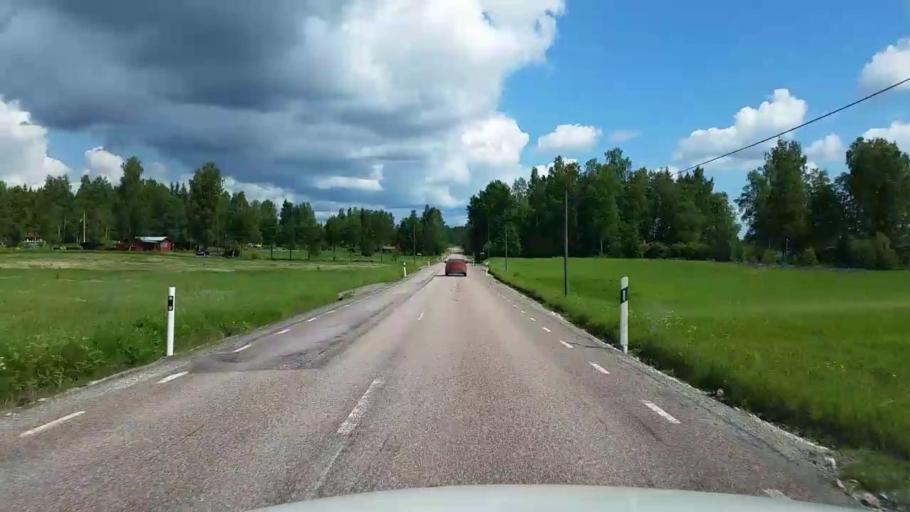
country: SE
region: Vaestmanland
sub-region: Skinnskattebergs Kommun
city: Skinnskatteberg
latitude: 59.7463
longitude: 15.8107
